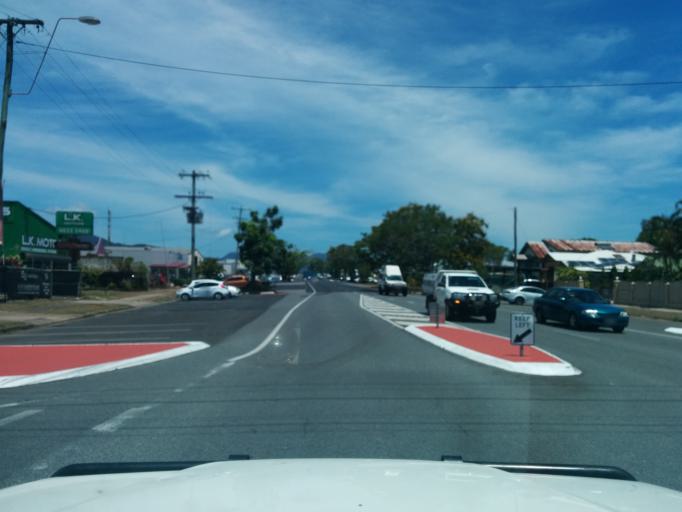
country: AU
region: Queensland
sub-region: Cairns
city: Cairns
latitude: -16.9338
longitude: 145.7648
